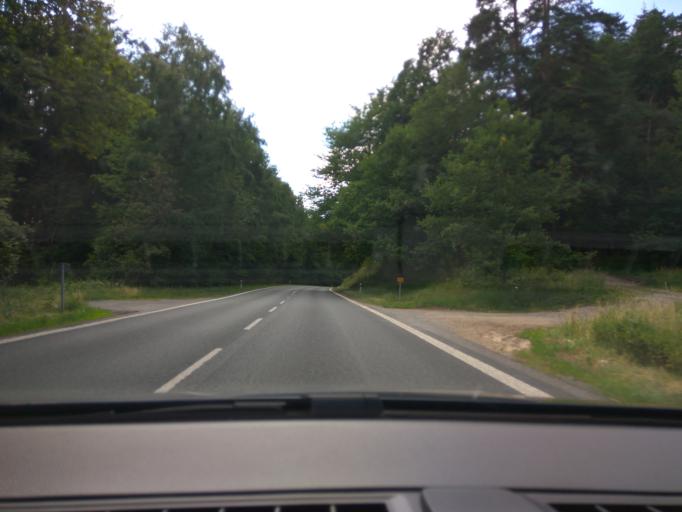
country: CZ
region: Jihocesky
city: Milevsko
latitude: 49.4643
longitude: 14.3175
